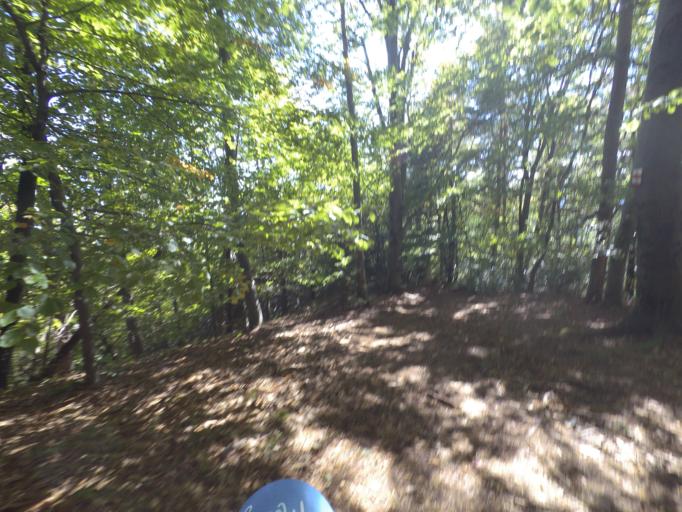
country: AT
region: Styria
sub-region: Politischer Bezirk Leibnitz
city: Kitzeck im Sausal
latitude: 46.7835
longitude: 15.4313
